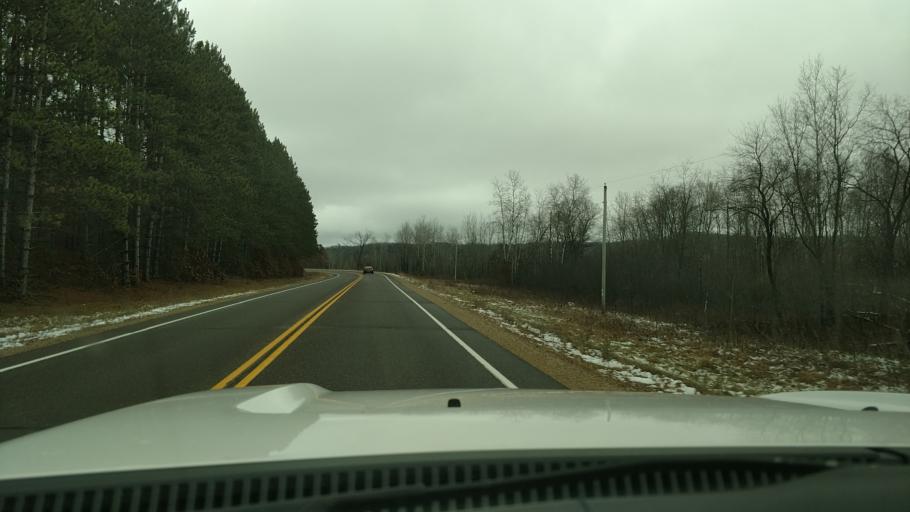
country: US
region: Wisconsin
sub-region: Dunn County
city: Boyceville
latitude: 45.1331
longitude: -92.0172
